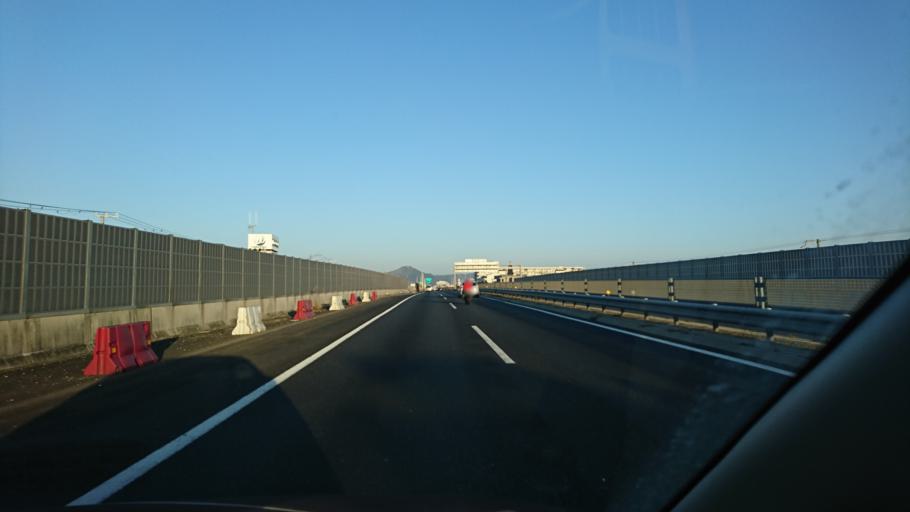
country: JP
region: Hyogo
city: Kakogawacho-honmachi
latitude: 34.7669
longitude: 134.8489
